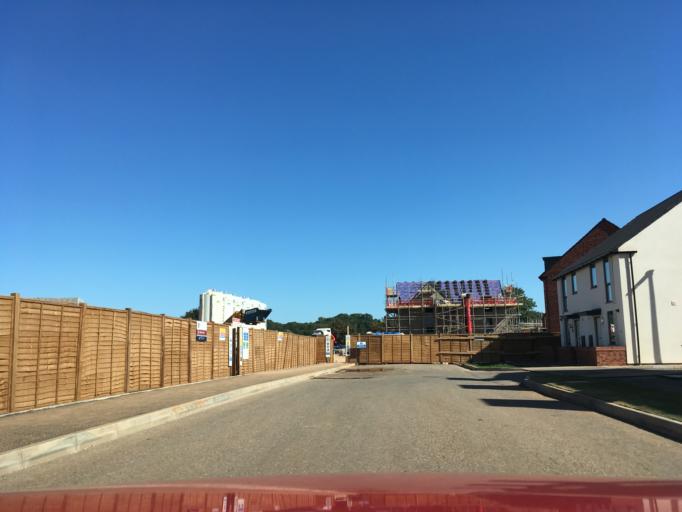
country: GB
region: England
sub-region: South Gloucestershire
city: Yate
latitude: 51.5593
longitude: -2.4159
